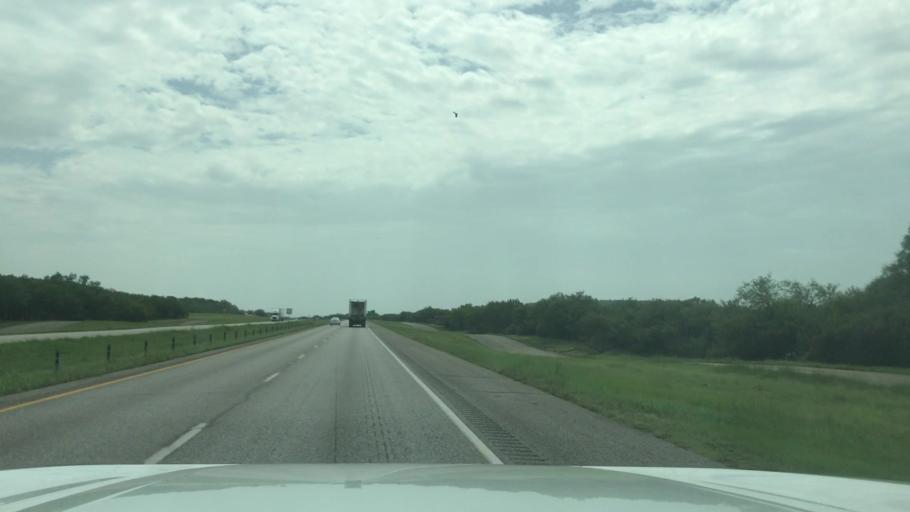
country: US
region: Texas
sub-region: Callahan County
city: Baird
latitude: 32.3716
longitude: -99.2225
